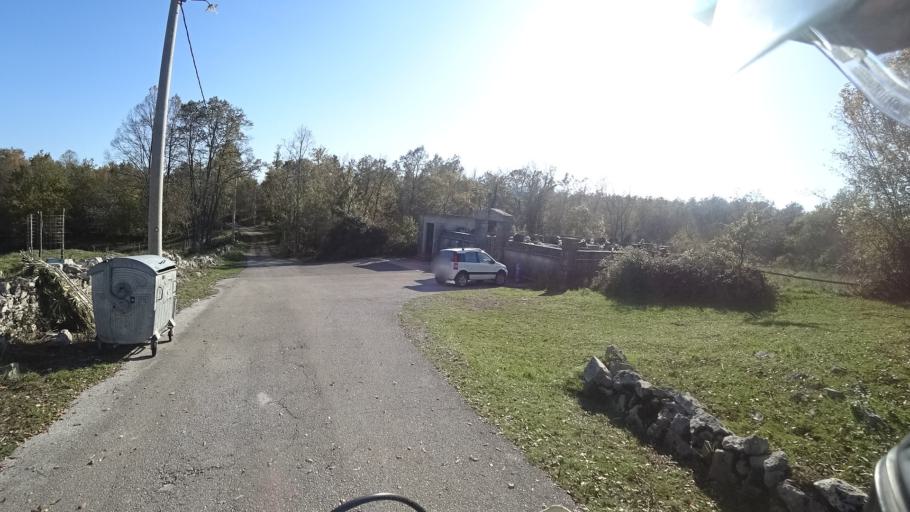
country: HR
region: Primorsko-Goranska
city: Klana
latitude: 45.4206
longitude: 14.3449
